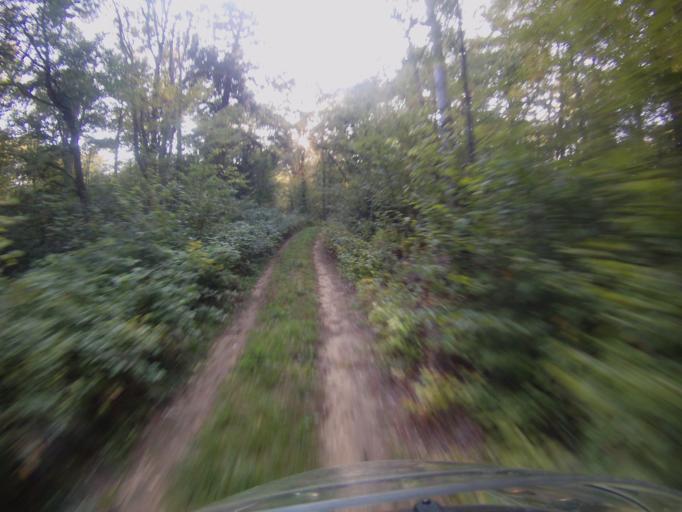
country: US
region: Vermont
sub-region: Addison County
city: Bristol
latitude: 44.0074
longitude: -73.0030
